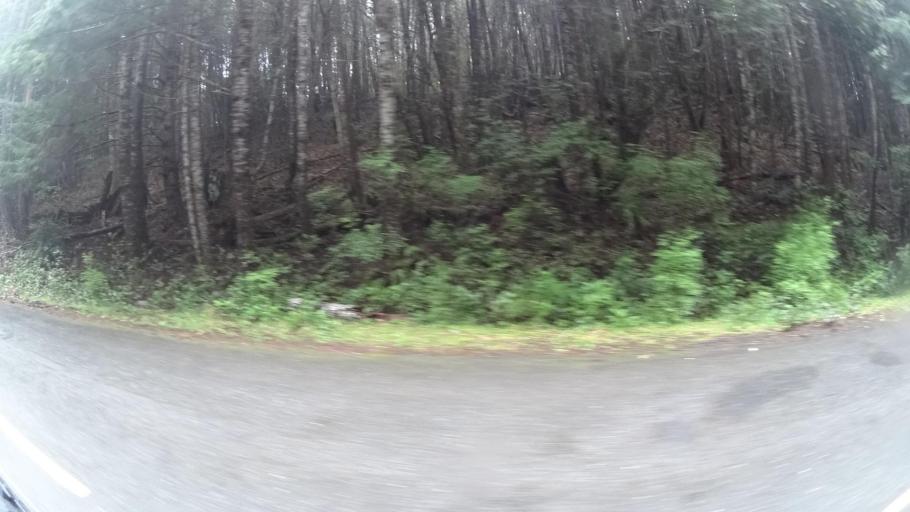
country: US
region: California
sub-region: Humboldt County
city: Westhaven-Moonstone
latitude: 41.2517
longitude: -123.9860
